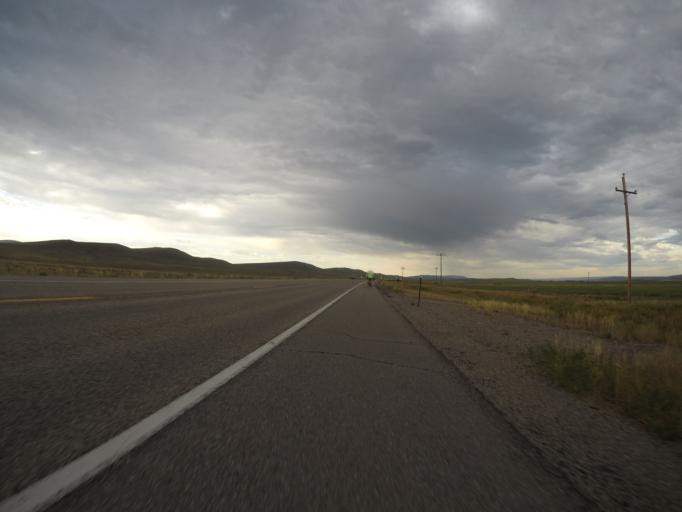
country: US
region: Utah
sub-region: Rich County
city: Randolph
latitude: 41.9112
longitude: -110.9551
